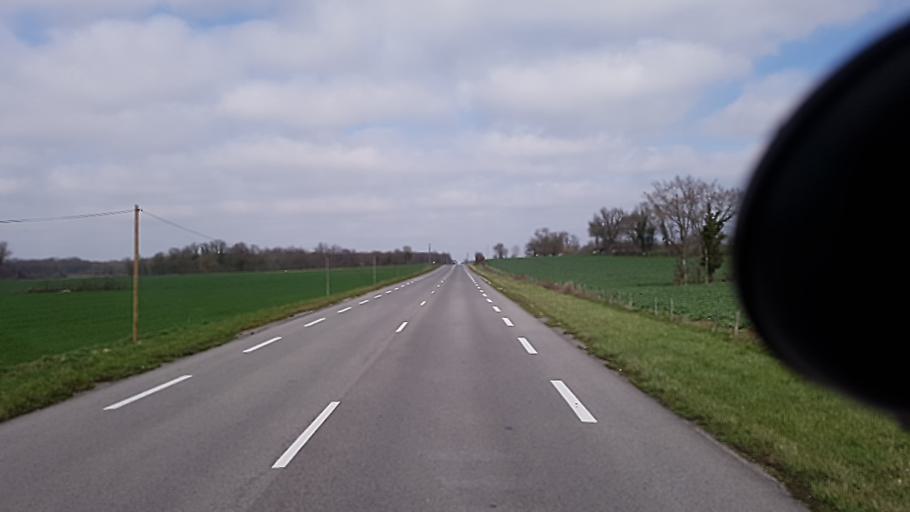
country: FR
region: Rhone-Alpes
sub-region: Departement de l'Ain
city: Villars-les-Dombes
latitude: 46.0231
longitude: 5.0571
